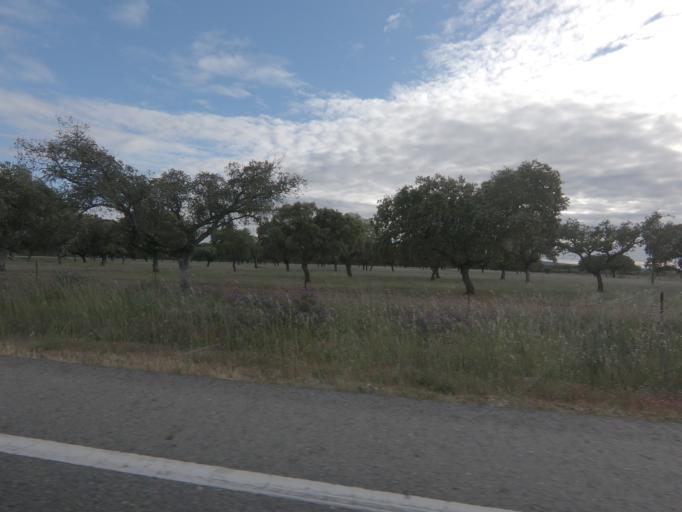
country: ES
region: Extremadura
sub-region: Provincia de Caceres
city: Torrejoncillo
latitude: 39.8708
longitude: -6.4410
